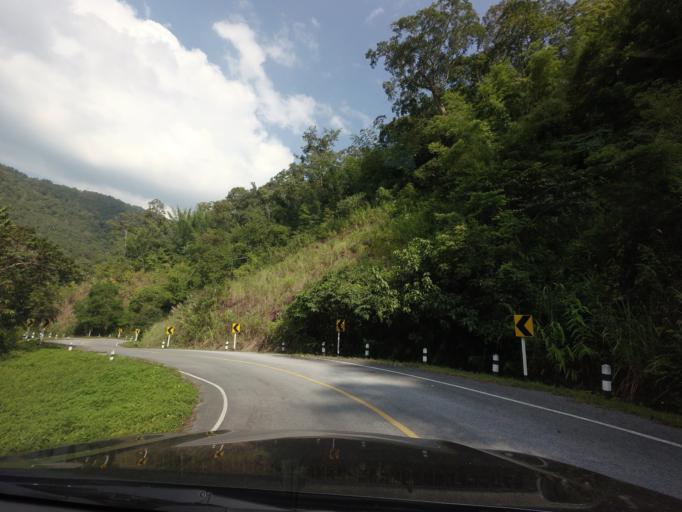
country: TH
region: Uttaradit
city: Ban Khok
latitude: 18.2460
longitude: 101.0002
